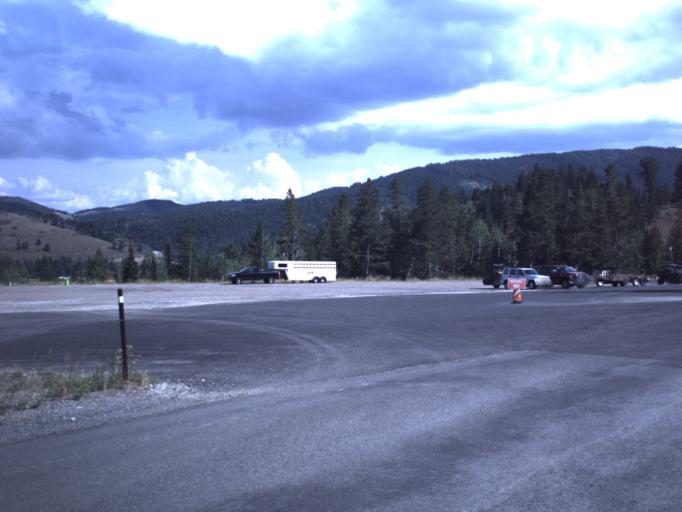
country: US
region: Utah
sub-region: Cache County
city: Richmond
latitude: 41.9699
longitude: -111.5402
